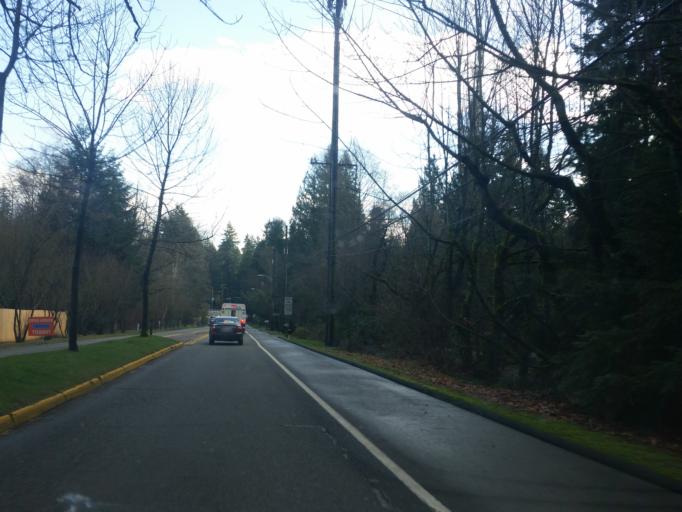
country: US
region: Washington
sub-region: King County
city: Lake Forest Park
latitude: 47.7654
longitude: -122.2956
